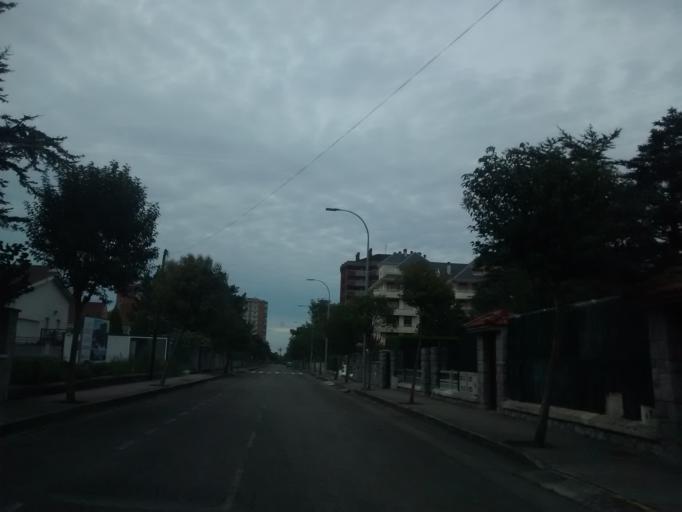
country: ES
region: Cantabria
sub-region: Provincia de Cantabria
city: Santona
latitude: 43.4225
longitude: -3.4458
